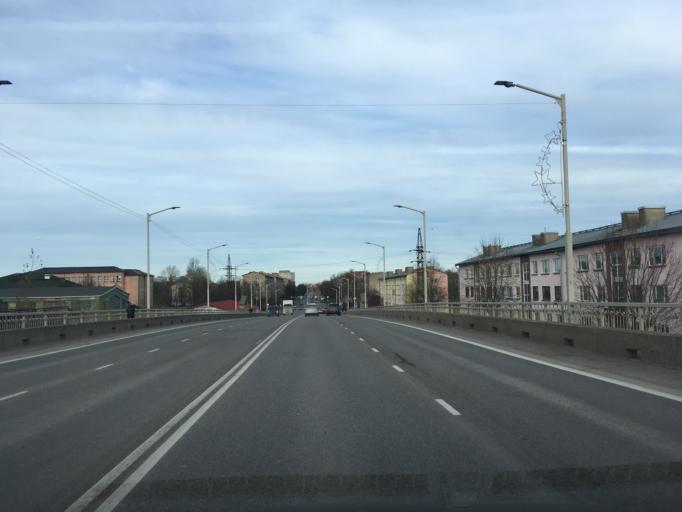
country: EE
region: Ida-Virumaa
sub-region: Narva linn
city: Narva
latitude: 59.3721
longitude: 28.1836
